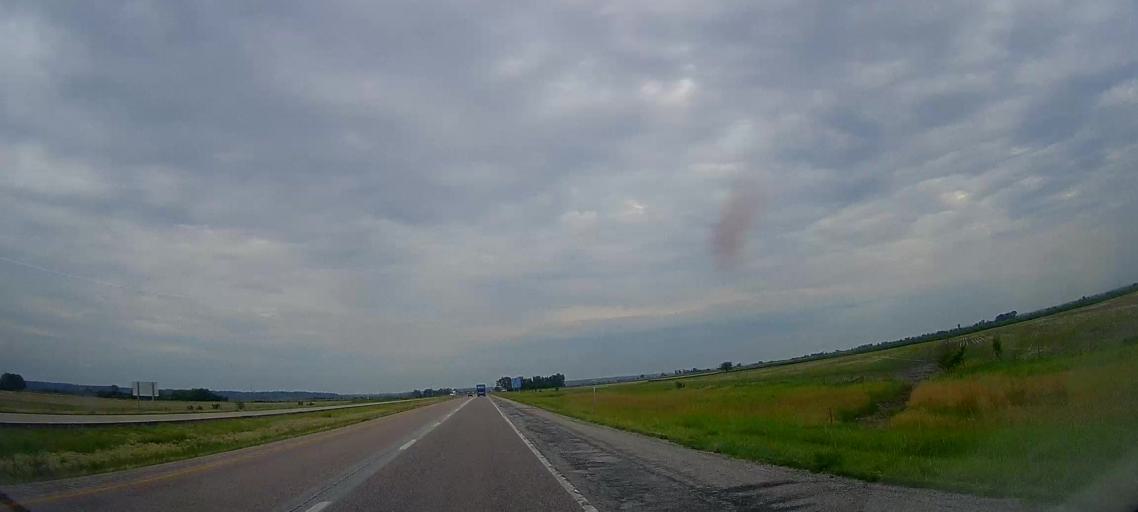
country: US
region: Iowa
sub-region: Harrison County
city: Missouri Valley
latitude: 41.5998
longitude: -95.9615
